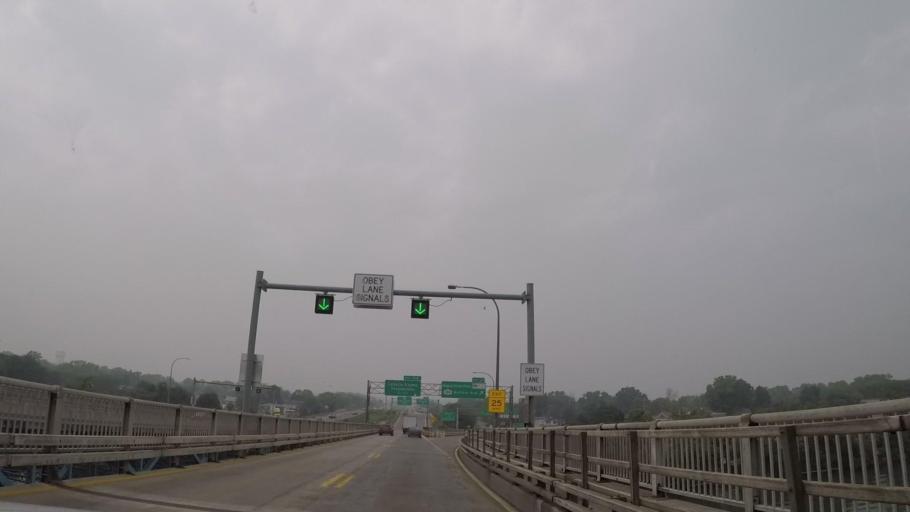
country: US
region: New York
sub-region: Niagara County
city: Niagara Falls
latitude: 43.0734
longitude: -78.9906
